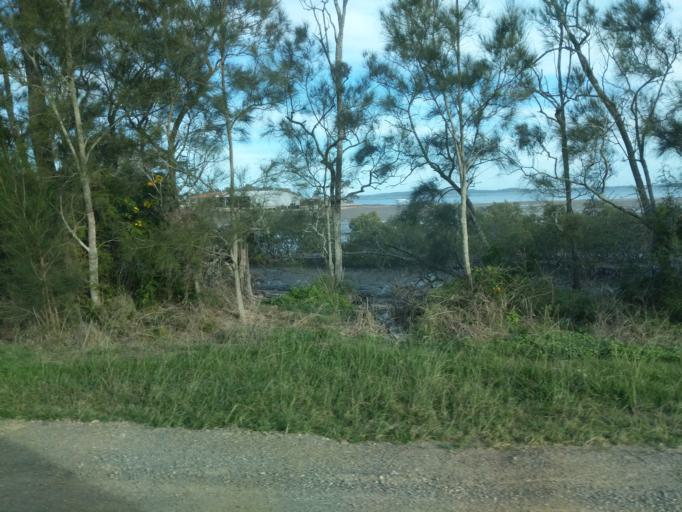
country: AU
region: New South Wales
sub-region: Port Stephens Shire
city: Port Stephens
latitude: -32.6670
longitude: 152.0120
